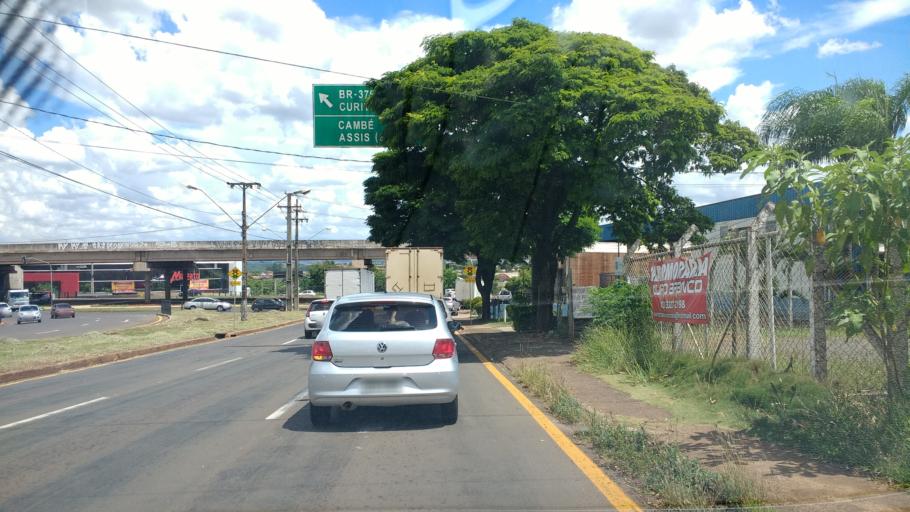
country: BR
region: Parana
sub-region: Londrina
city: Londrina
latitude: -23.3596
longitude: -51.1514
